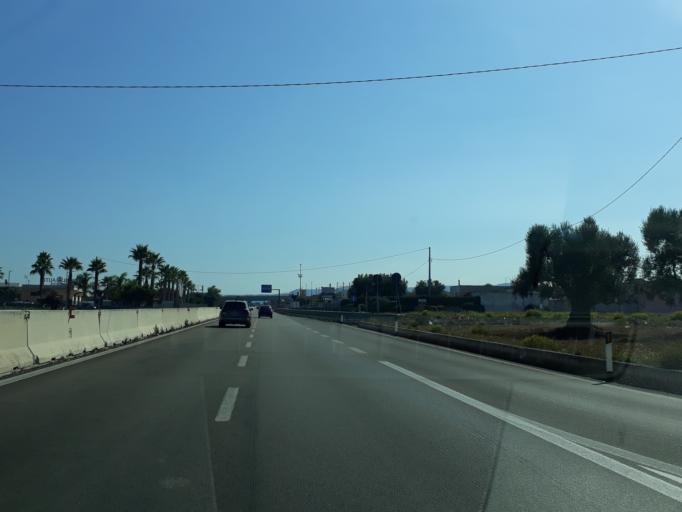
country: IT
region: Apulia
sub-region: Provincia di Brindisi
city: Fasano
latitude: 40.8545
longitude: 17.3536
